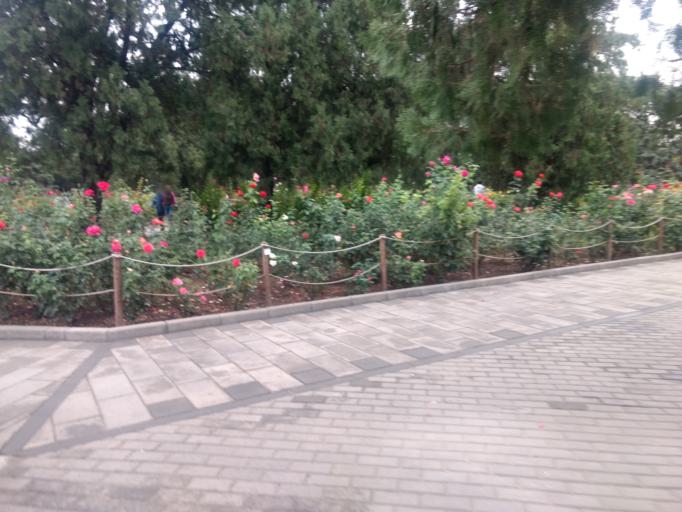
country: CN
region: Beijing
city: Longtan
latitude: 39.8808
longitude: 116.4032
